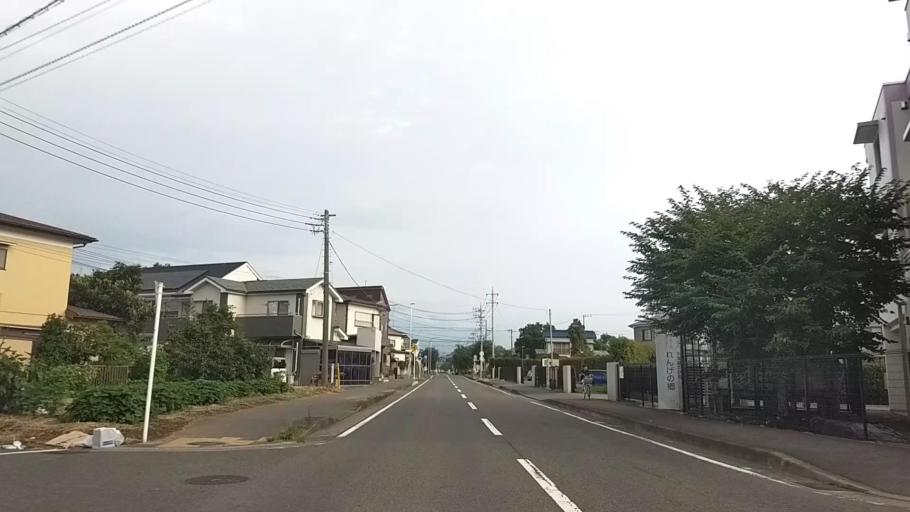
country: JP
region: Kanagawa
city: Oiso
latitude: 35.3462
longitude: 139.3049
